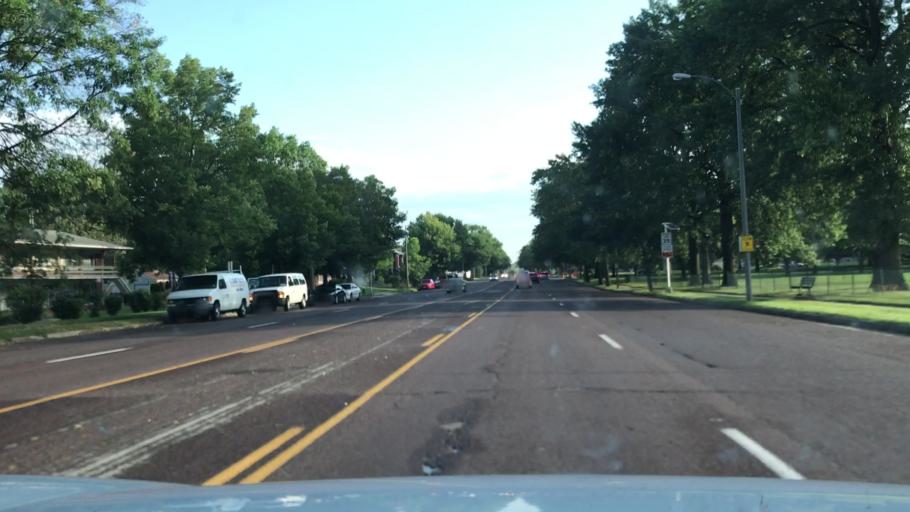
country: US
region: Missouri
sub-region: Saint Louis County
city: Maplewood
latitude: 38.5966
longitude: -90.3089
